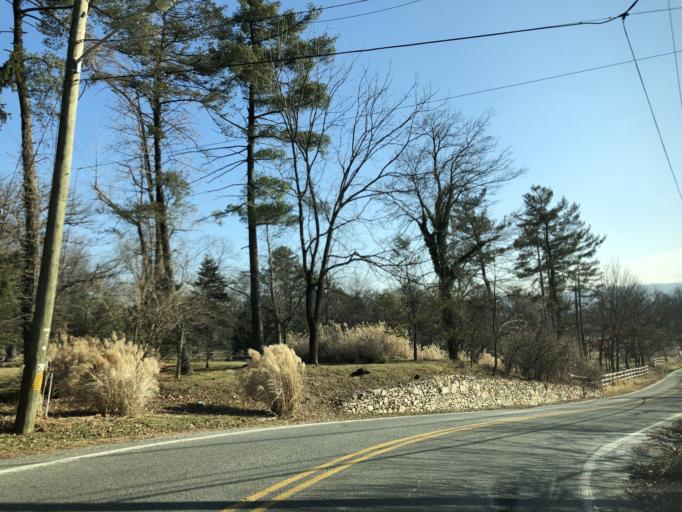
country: US
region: Pennsylvania
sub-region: Chester County
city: Chesterbrook
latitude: 40.0801
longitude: -75.4859
